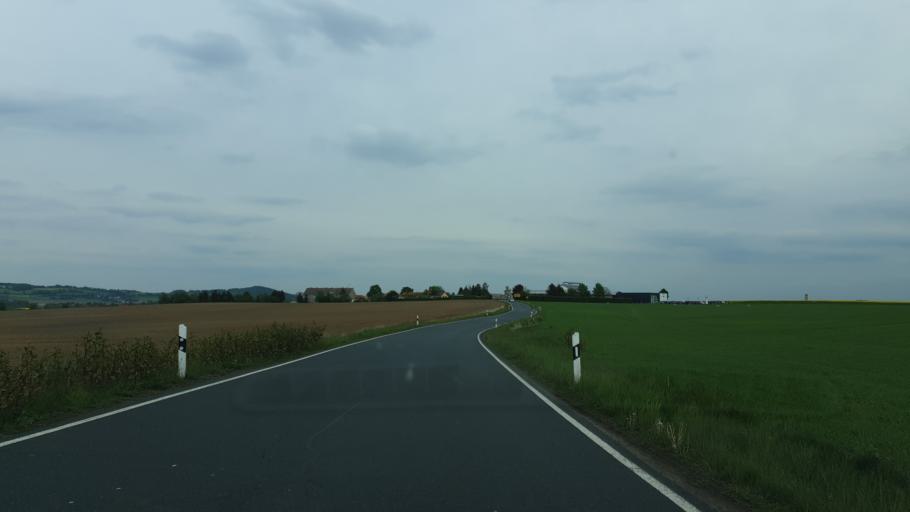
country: DE
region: Saxony
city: Dippoldiswalde
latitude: 50.9082
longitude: 13.6856
